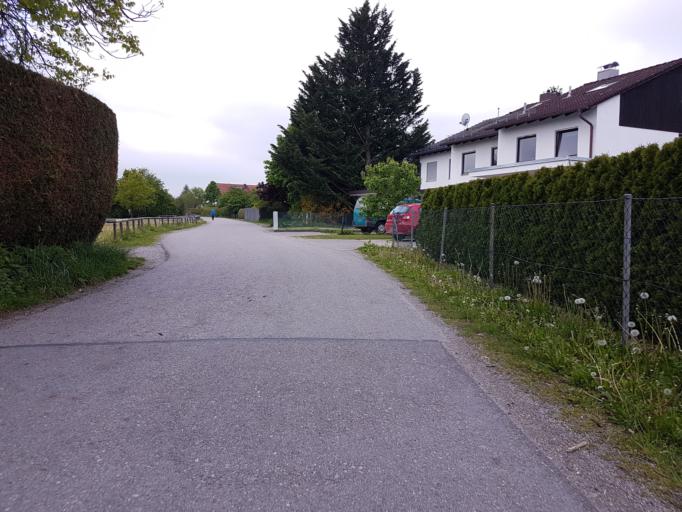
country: DE
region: Bavaria
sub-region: Upper Bavaria
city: Karlsfeld
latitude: 48.1912
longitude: 11.4544
